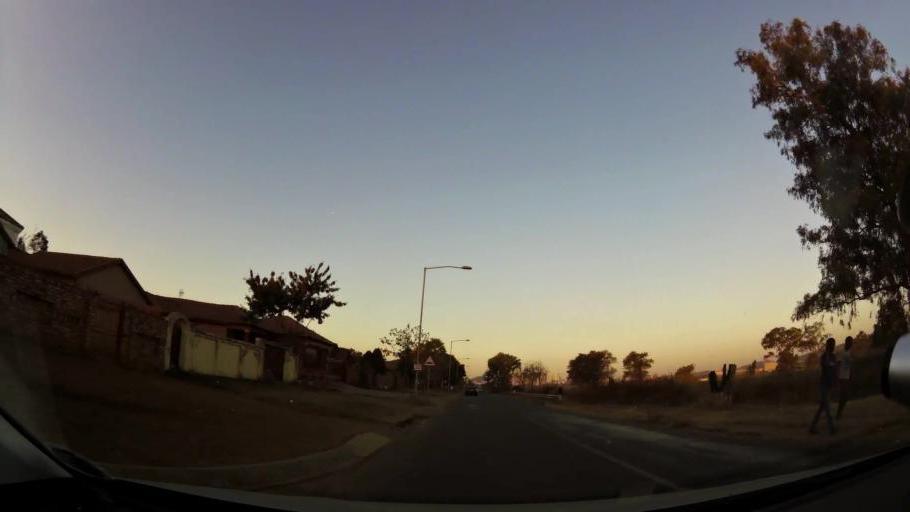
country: ZA
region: Gauteng
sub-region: City of Tshwane Metropolitan Municipality
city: Pretoria
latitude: -25.7432
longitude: 28.1461
